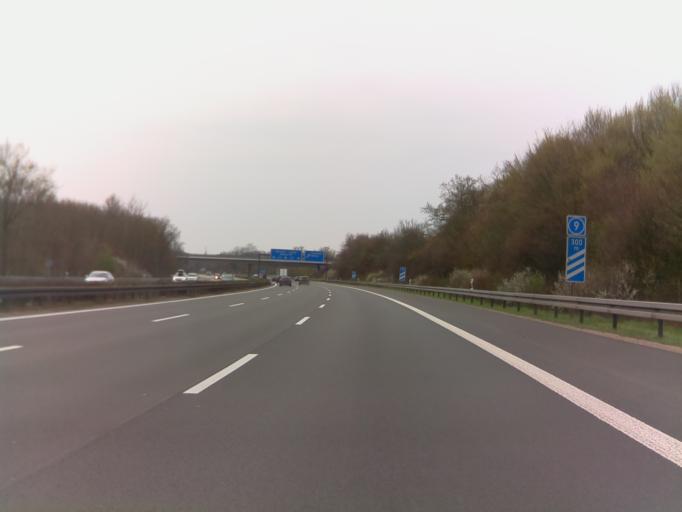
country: DE
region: Saxony-Anhalt
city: Vockerode
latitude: 51.8507
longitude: 12.3320
